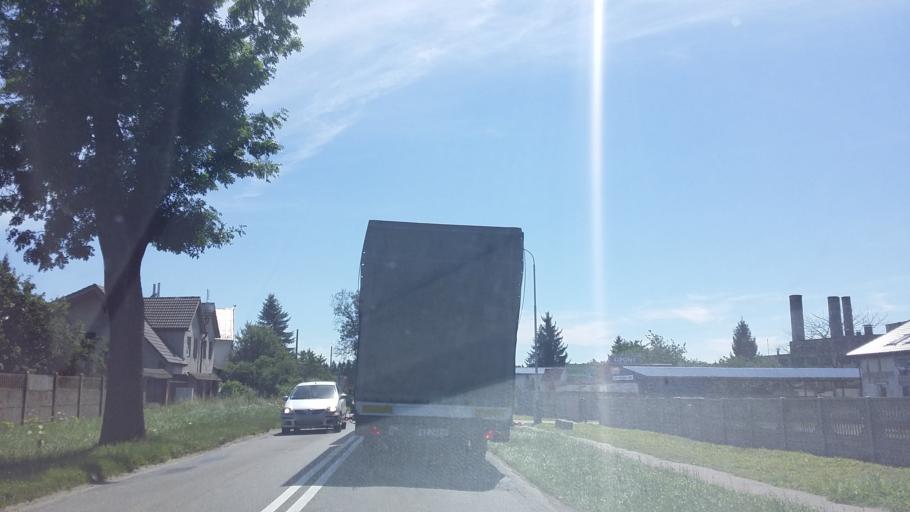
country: PL
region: West Pomeranian Voivodeship
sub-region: Powiat lobeski
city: Lobez
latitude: 53.6245
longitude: 15.6124
